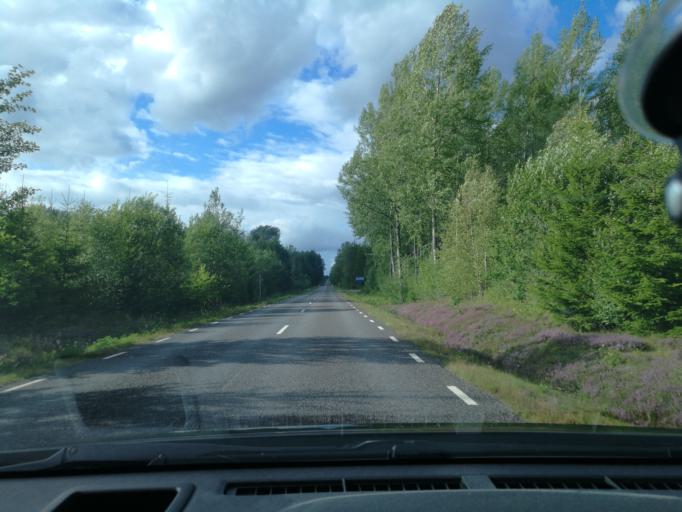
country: SE
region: Kronoberg
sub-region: Vaxjo Kommun
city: Braas
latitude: 57.0826
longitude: 15.0016
